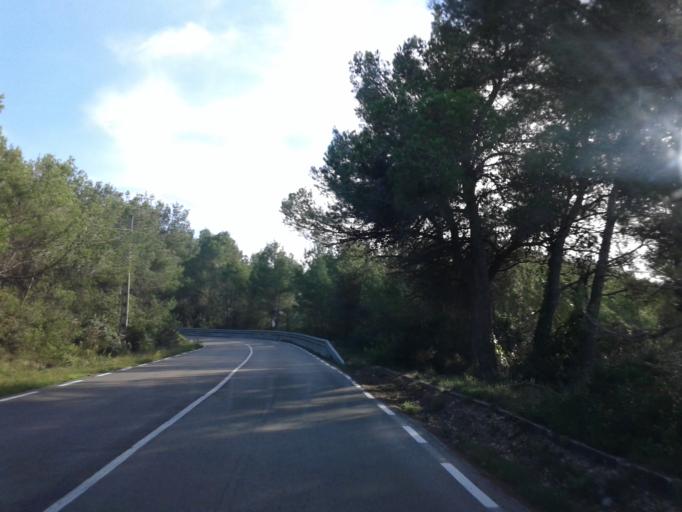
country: ES
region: Catalonia
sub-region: Provincia de Barcelona
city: Vilafranca del Penedes
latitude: 41.3065
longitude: 1.6916
